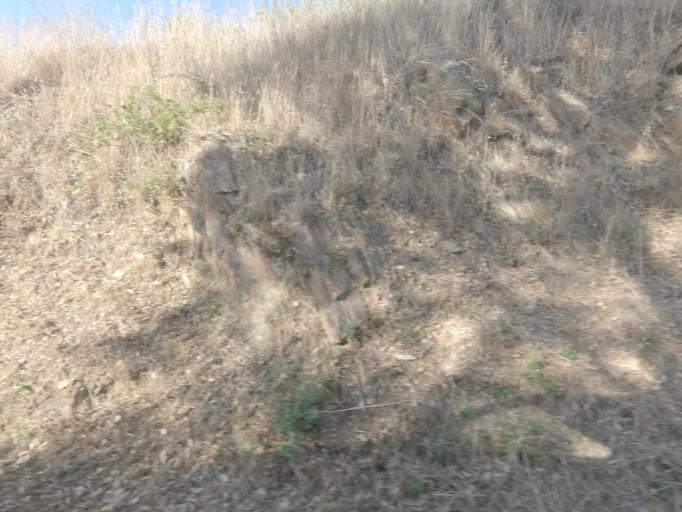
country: PT
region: Vila Real
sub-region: Sabrosa
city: Sabrosa
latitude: 41.2390
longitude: -7.5214
